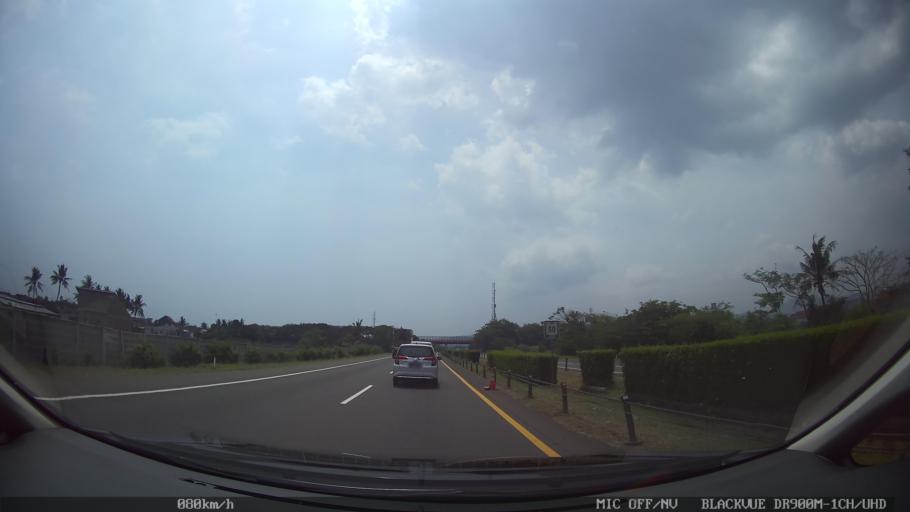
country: ID
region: Banten
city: Bojonegara
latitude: -6.0069
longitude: 106.0682
